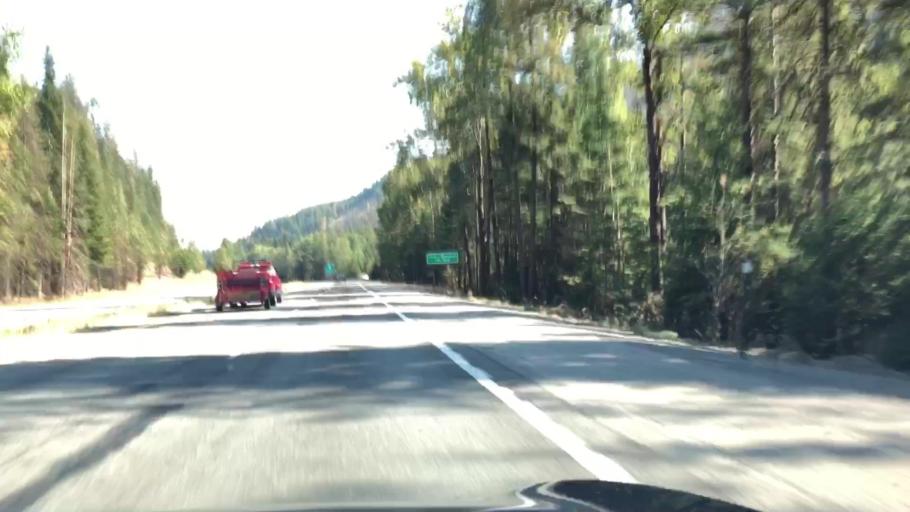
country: US
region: Idaho
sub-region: Shoshone County
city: Pinehurst
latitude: 47.5841
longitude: -116.4712
